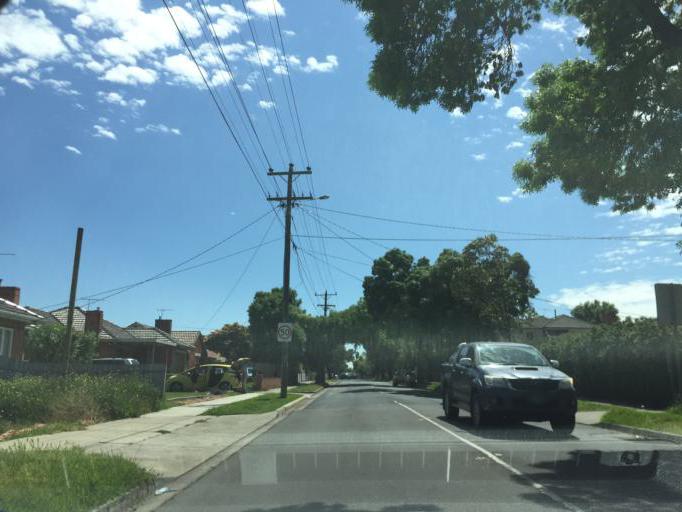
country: AU
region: Victoria
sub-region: Maribyrnong
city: Braybrook
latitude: -37.7899
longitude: 144.8454
